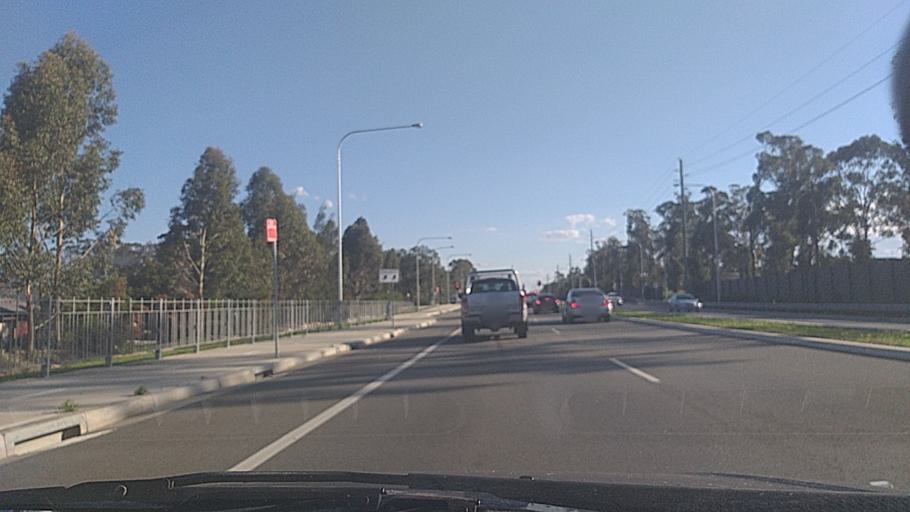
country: AU
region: New South Wales
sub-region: Penrith Municipality
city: Werrington Downs
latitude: -33.7260
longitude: 150.7210
